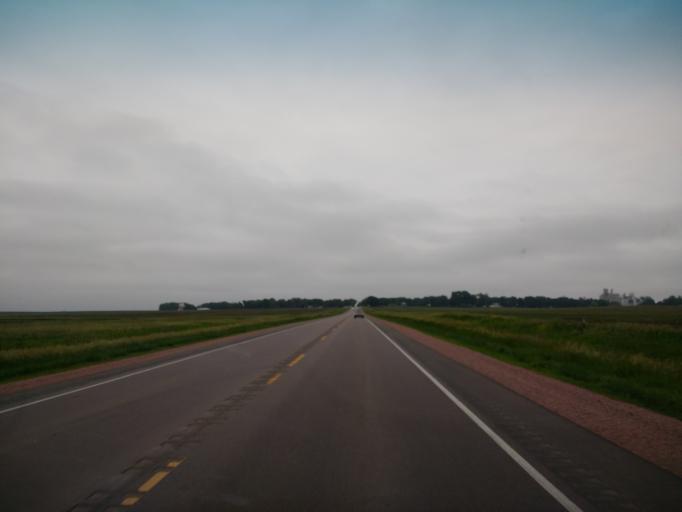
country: US
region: Iowa
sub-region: O'Brien County
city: Sanborn
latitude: 43.1861
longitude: -95.6755
